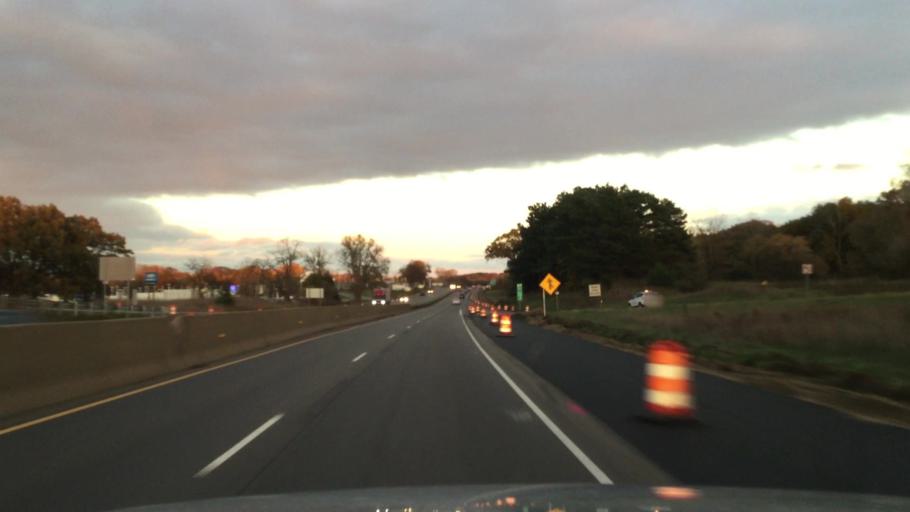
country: US
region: Michigan
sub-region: Jackson County
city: Jackson
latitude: 42.2755
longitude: -84.3825
